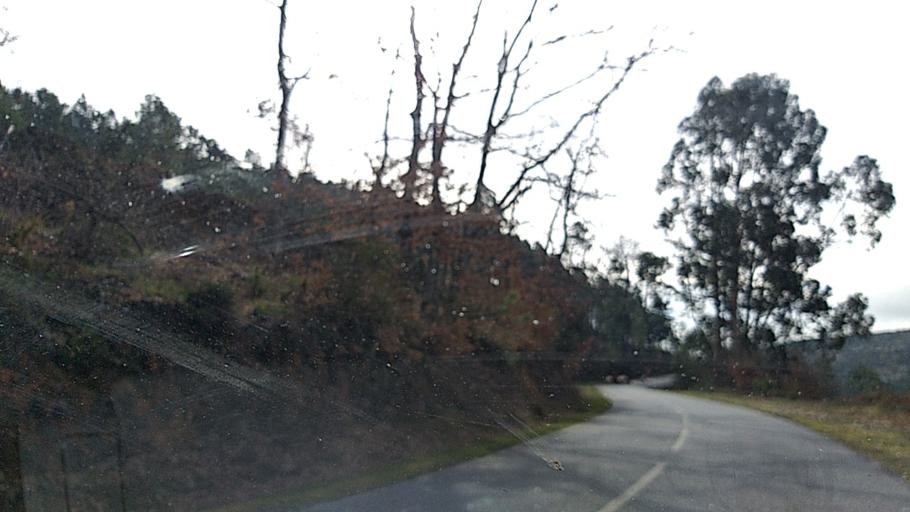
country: PT
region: Guarda
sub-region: Fornos de Algodres
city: Fornos de Algodres
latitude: 40.6881
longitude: -7.5411
